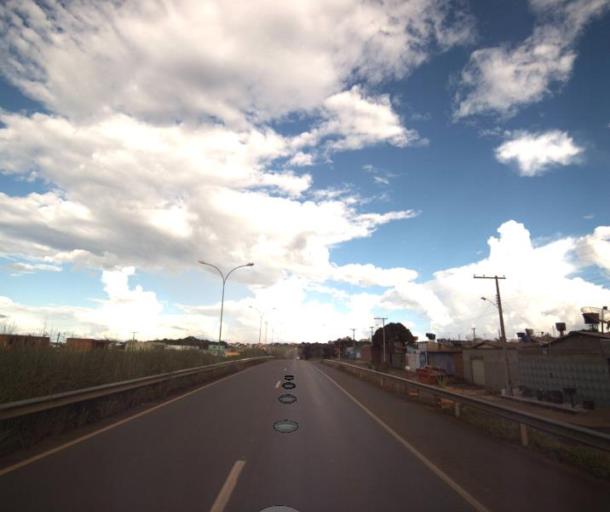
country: BR
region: Goias
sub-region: Anapolis
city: Anapolis
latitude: -16.2774
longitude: -48.9651
